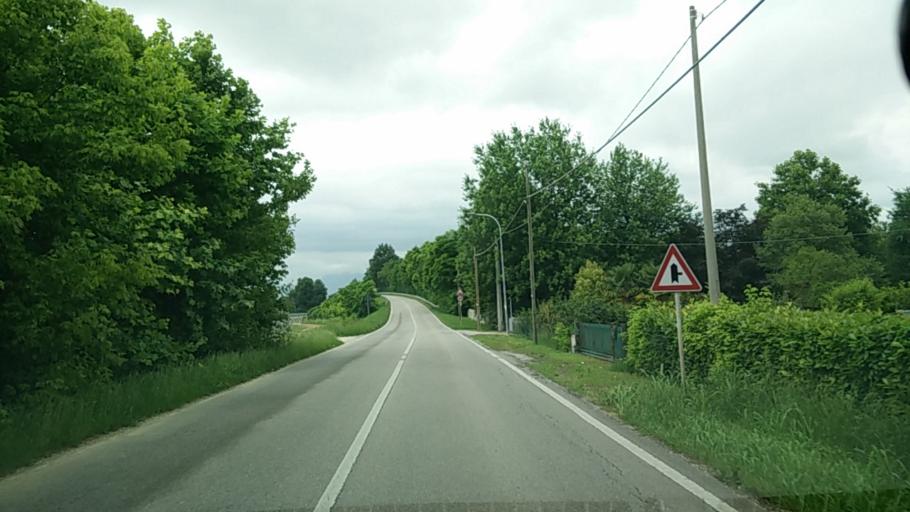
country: IT
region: Veneto
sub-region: Provincia di Treviso
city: Mareno di Piave
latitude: 45.8549
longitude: 12.3373
